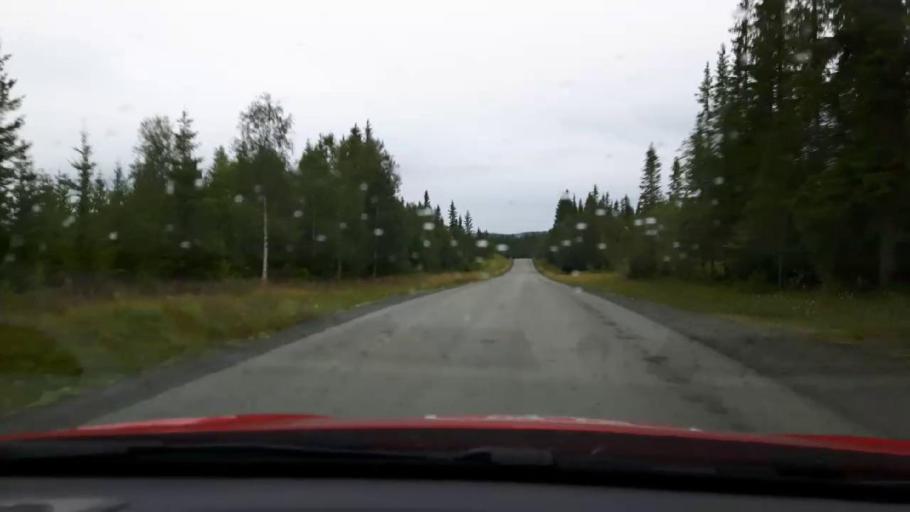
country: SE
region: Jaemtland
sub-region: Are Kommun
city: Are
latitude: 63.4571
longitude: 13.2018
